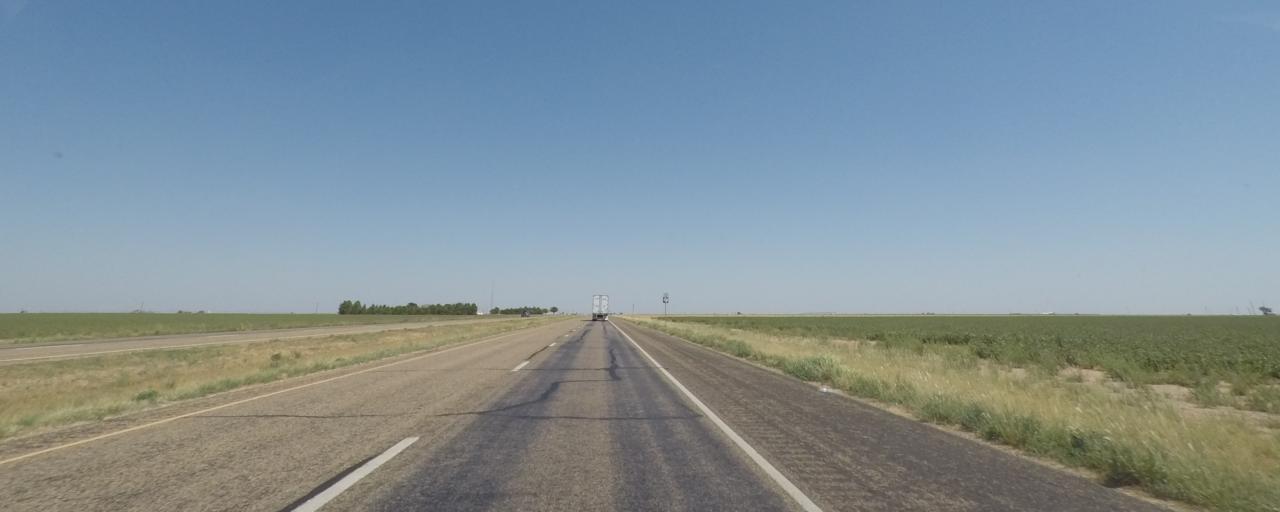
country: US
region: Texas
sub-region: Crosby County
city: Ralls
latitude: 33.6697
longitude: -101.3485
